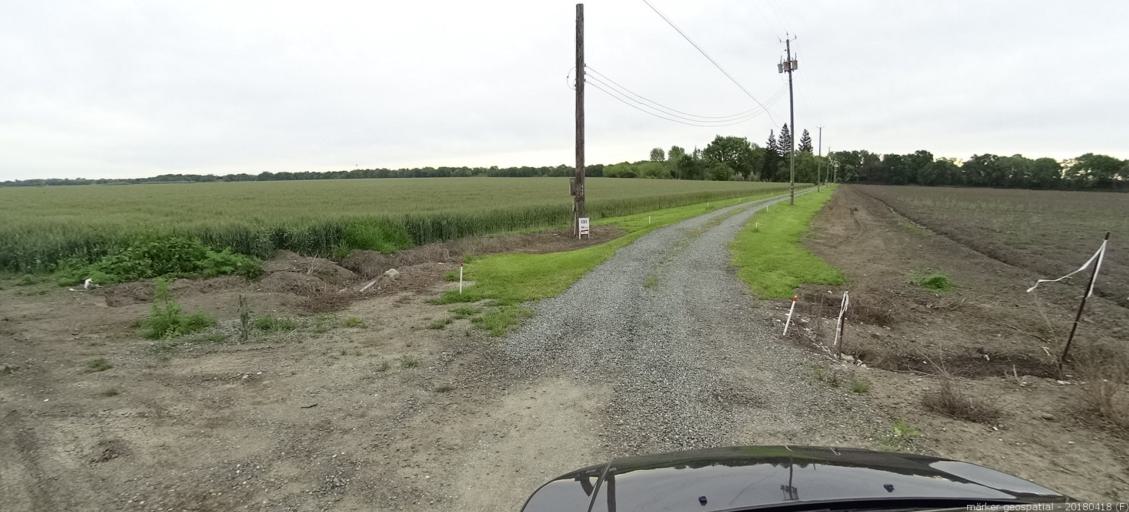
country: US
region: California
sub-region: Sacramento County
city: Laguna
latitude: 38.4124
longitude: -121.5093
